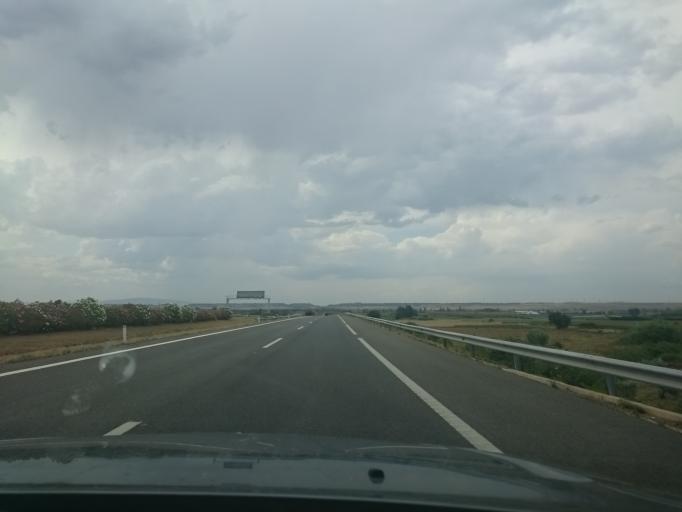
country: ES
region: Navarre
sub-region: Provincia de Navarra
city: Murchante
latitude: 42.0364
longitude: -1.6441
